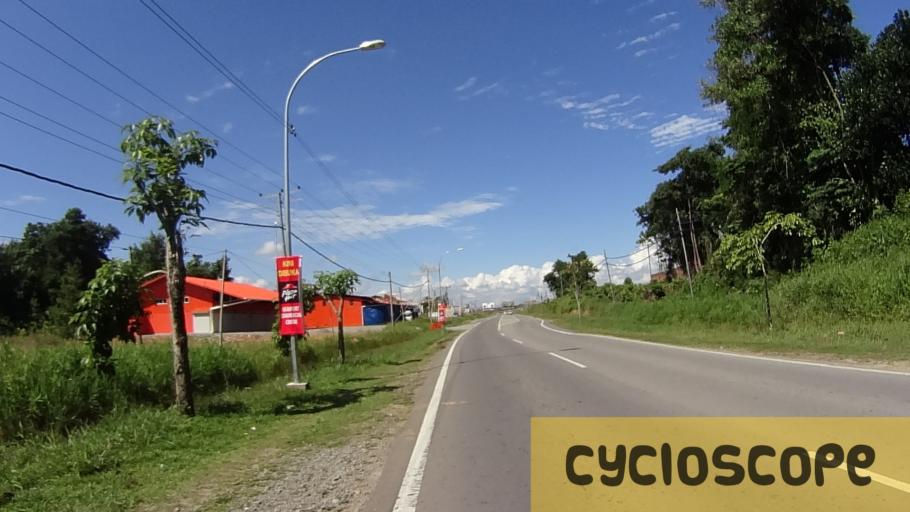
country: MY
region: Sabah
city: Beaufort
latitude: 5.3426
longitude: 115.7337
